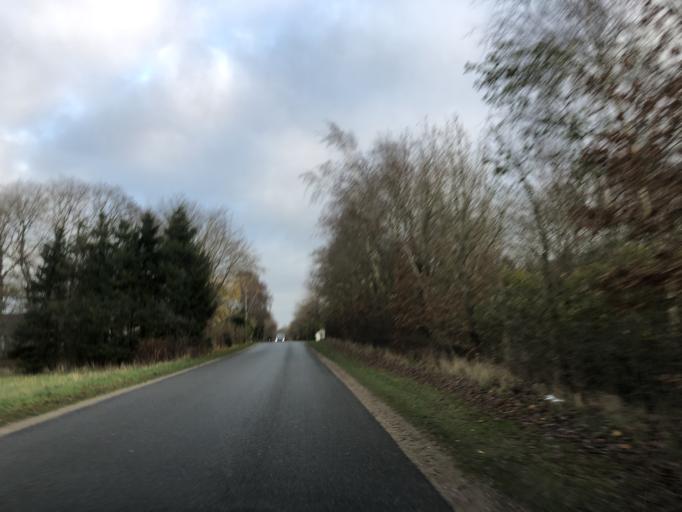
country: DK
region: Central Jutland
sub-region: Viborg Kommune
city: Viborg
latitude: 56.4756
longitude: 9.3429
